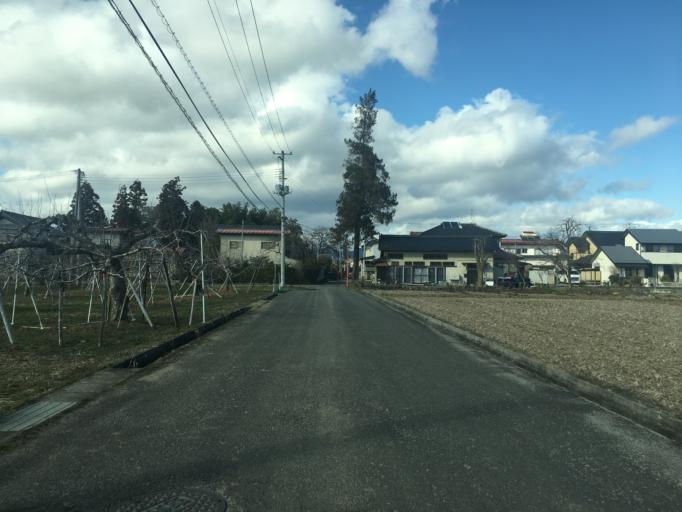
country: JP
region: Fukushima
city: Fukushima-shi
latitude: 37.7499
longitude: 140.4301
